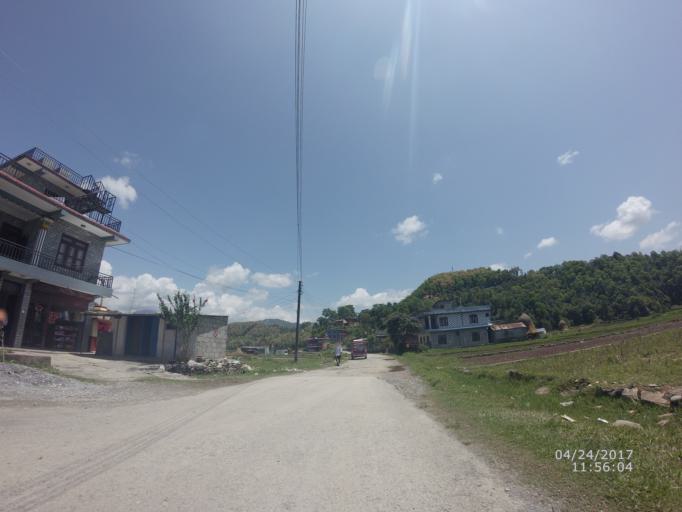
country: NP
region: Western Region
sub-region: Gandaki Zone
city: Pokhara
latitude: 28.1698
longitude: 84.0752
